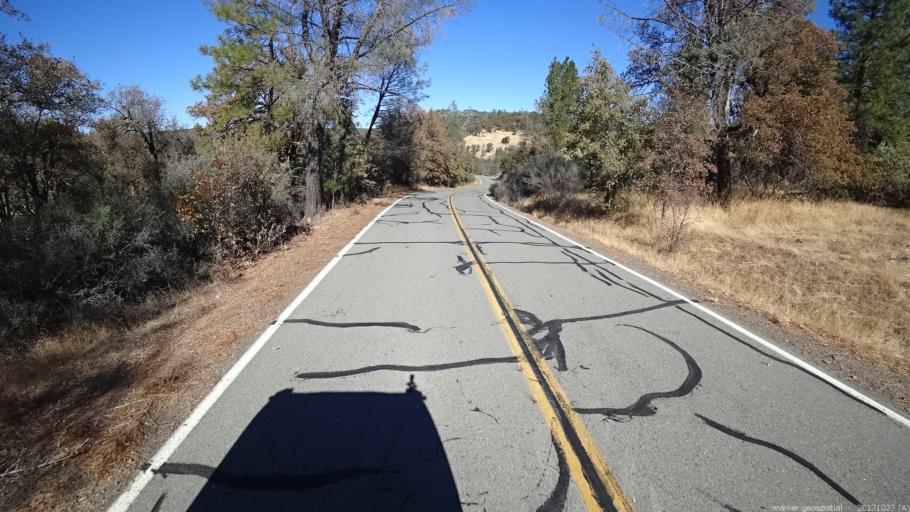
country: US
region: California
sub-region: Shasta County
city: Bella Vista
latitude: 40.7352
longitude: -122.0112
